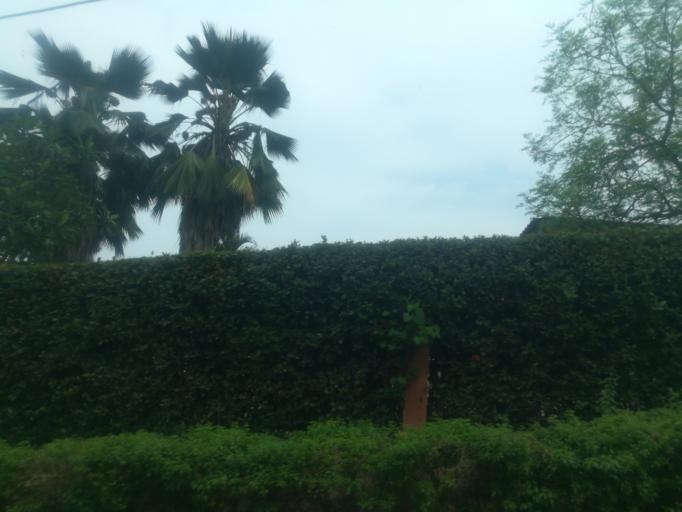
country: NG
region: Oyo
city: Ibadan
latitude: 7.4242
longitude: 3.9252
